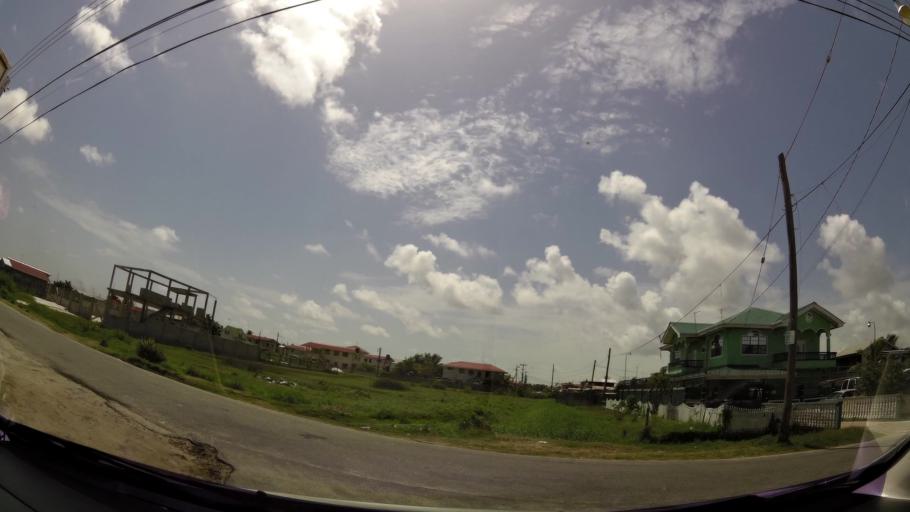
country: GY
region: Demerara-Mahaica
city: Mahaica Village
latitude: 6.7712
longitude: -58.0107
